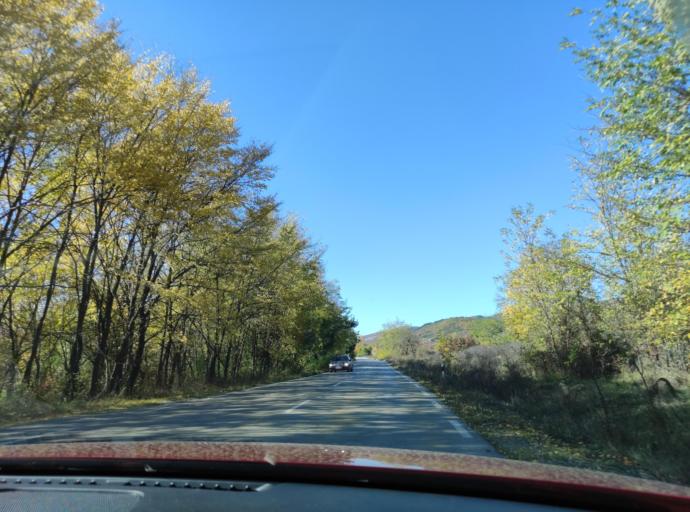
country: BG
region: Montana
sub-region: Obshtina Chiprovtsi
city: Chiprovtsi
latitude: 43.4263
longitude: 23.0071
